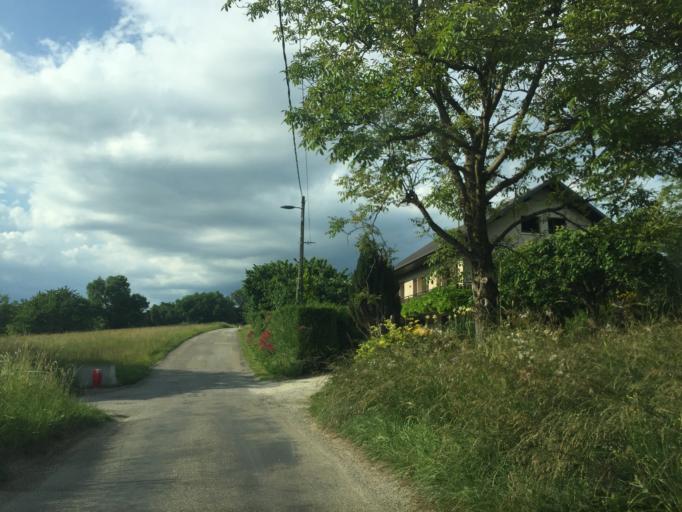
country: FR
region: Rhone-Alpes
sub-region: Departement de la Savoie
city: Drumettaz-Clarafond
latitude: 45.6681
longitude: 5.9332
